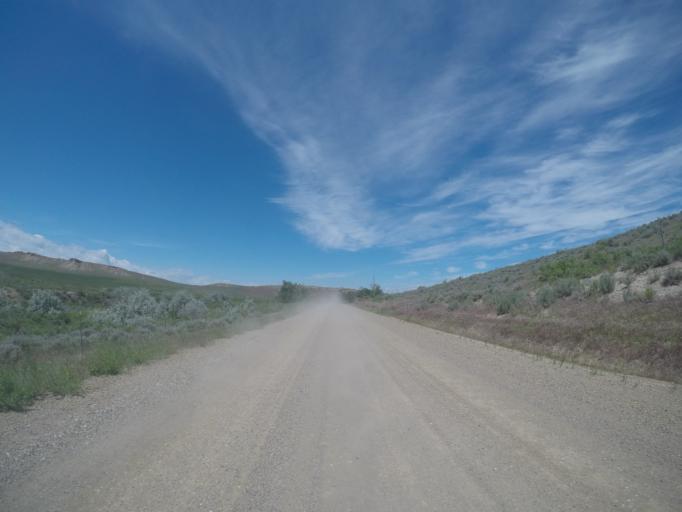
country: US
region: Montana
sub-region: Carbon County
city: Red Lodge
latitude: 45.2322
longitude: -108.8492
